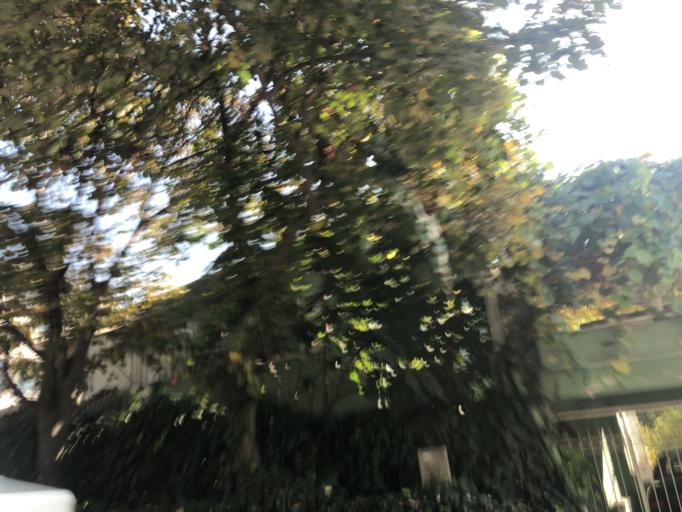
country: TR
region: Istanbul
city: UEskuedar
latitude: 41.0066
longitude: 29.0360
